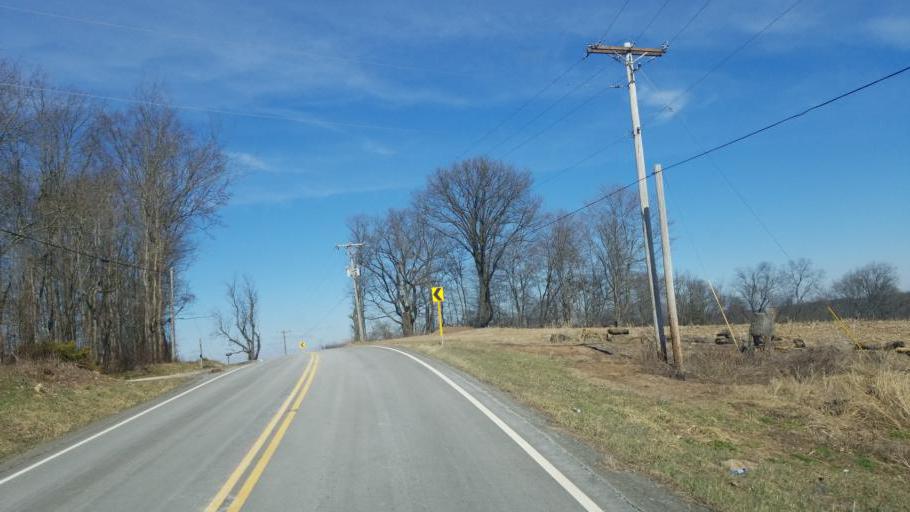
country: US
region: Ohio
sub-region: Knox County
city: Danville
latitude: 40.4926
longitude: -82.2206
